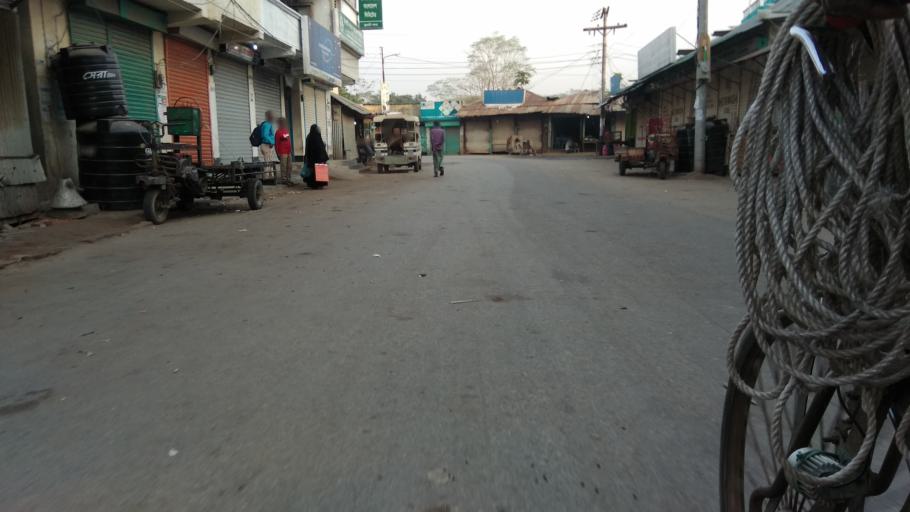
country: BD
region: Barisal
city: Mehendiganj
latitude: 22.9154
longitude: 90.4120
